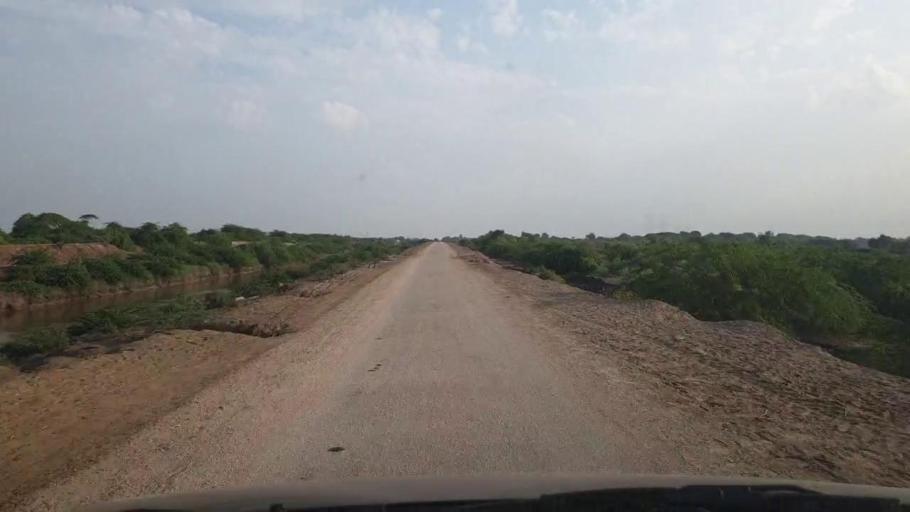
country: PK
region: Sindh
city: Badin
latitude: 24.5357
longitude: 68.6763
